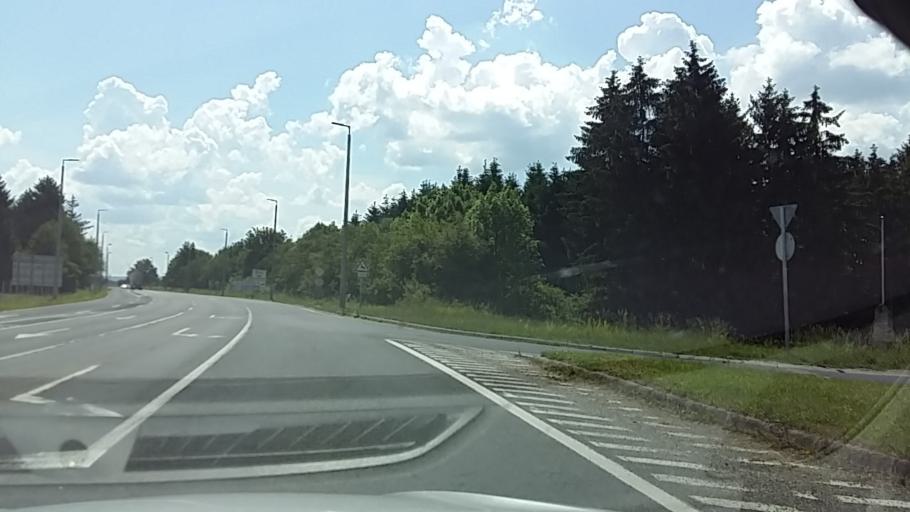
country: AT
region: Burgenland
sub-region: Politischer Bezirk Jennersdorf
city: Heiligenkreuz im Lafnitztal
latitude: 46.9802
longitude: 16.2835
